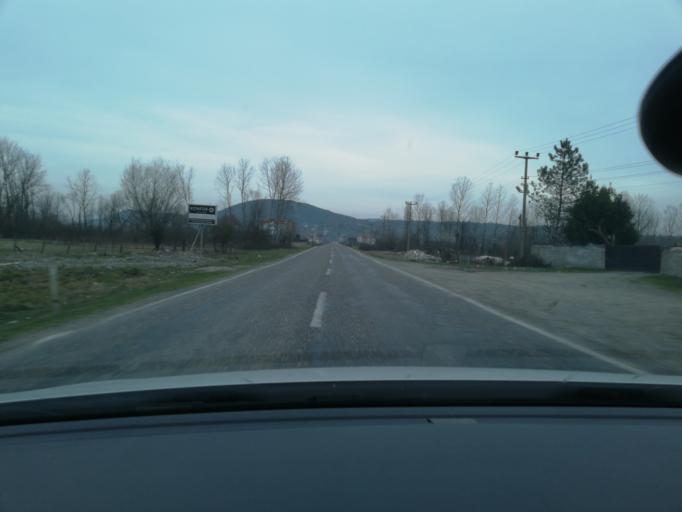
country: TR
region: Zonguldak
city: Saltukova
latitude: 41.5157
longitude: 32.1029
